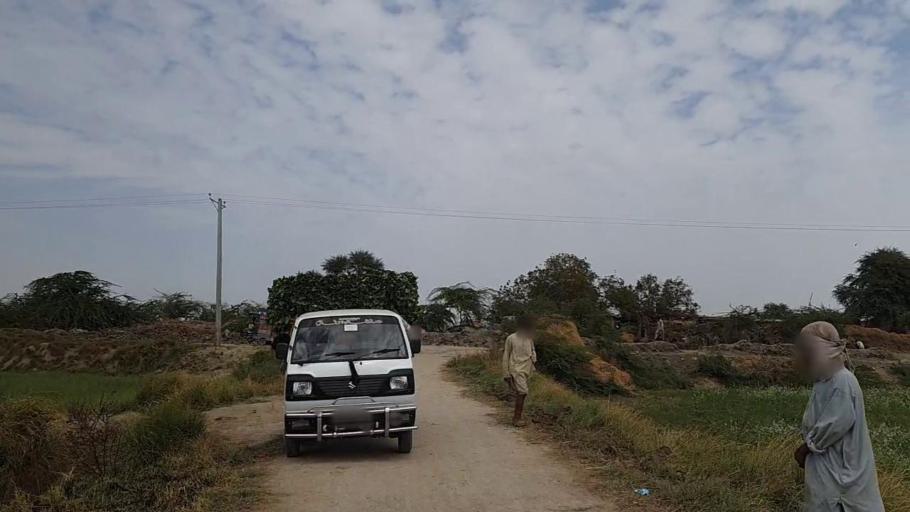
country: PK
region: Sindh
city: Daro Mehar
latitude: 24.7954
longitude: 68.2084
